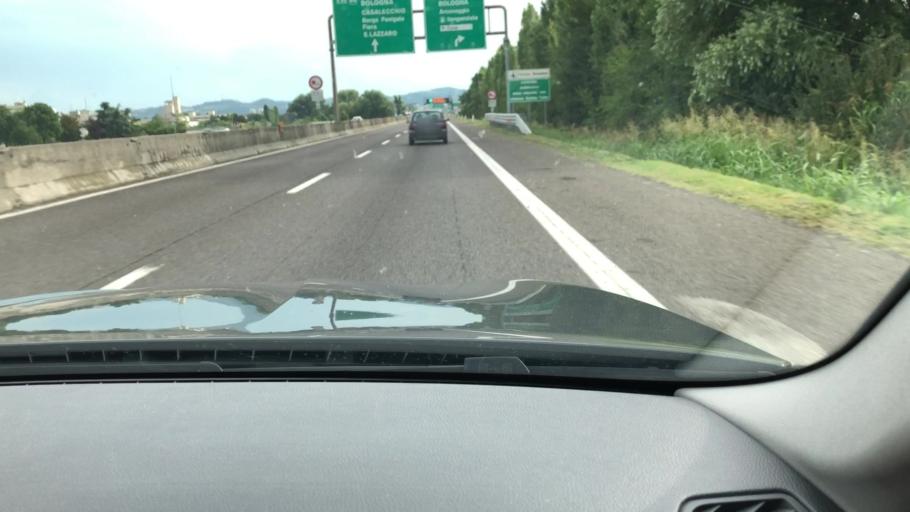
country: IT
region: Emilia-Romagna
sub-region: Provincia di Bologna
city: Progresso
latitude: 44.5419
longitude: 11.3675
